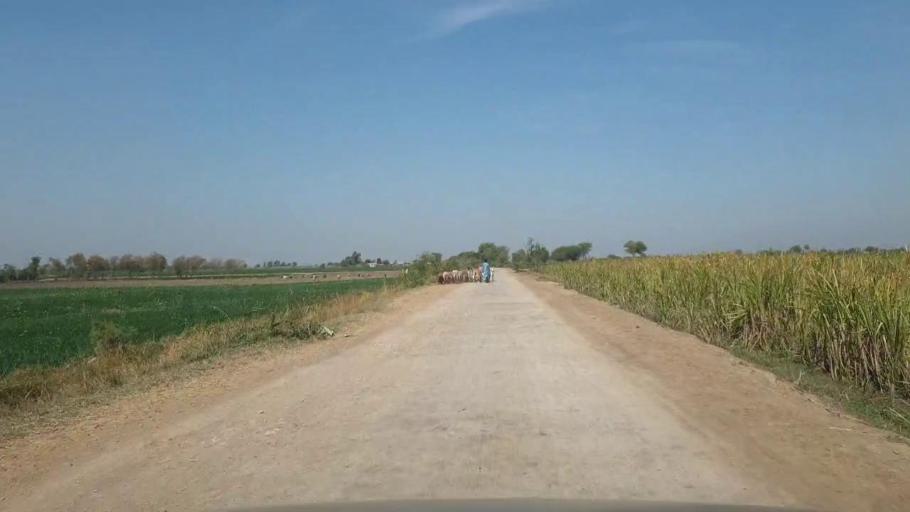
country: PK
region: Sindh
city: Mirwah Gorchani
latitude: 25.4369
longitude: 69.1651
